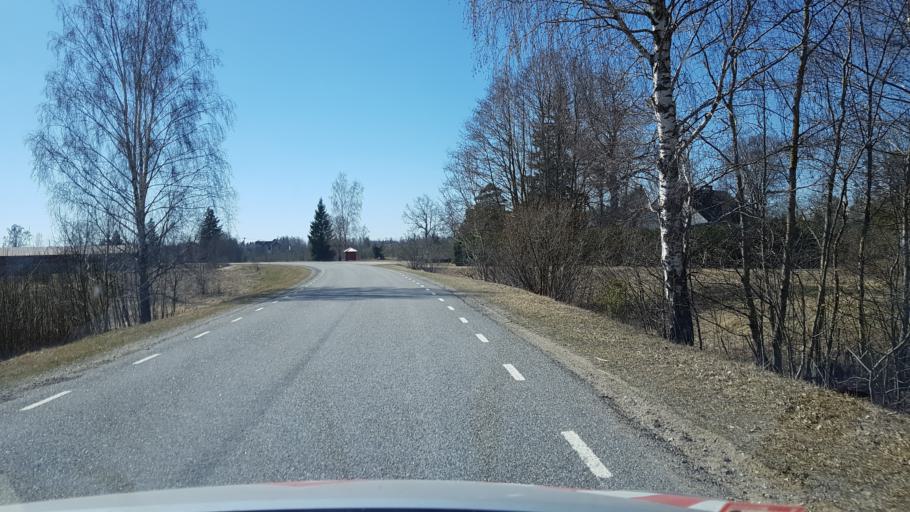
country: EE
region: Laeaene-Virumaa
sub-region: Rakke vald
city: Rakke
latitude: 58.9990
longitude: 26.2763
